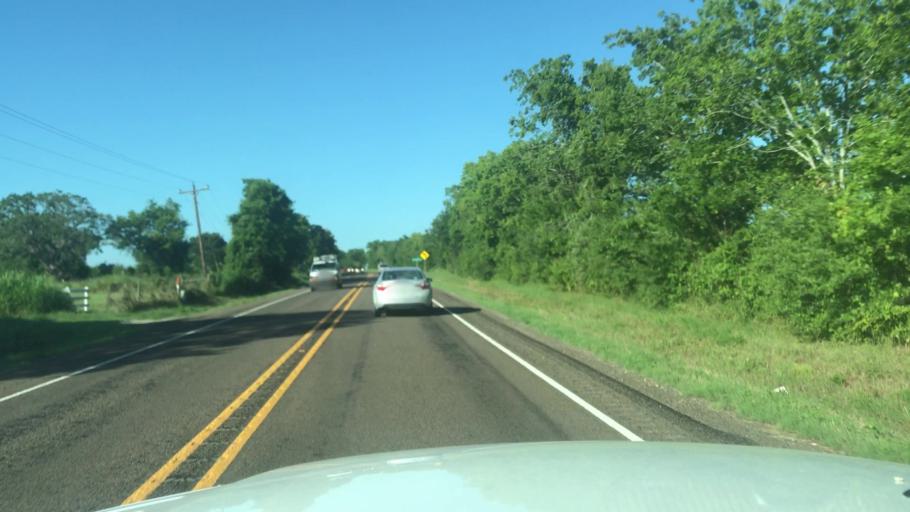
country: US
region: Texas
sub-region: Grimes County
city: Anderson
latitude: 30.6360
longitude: -95.8633
